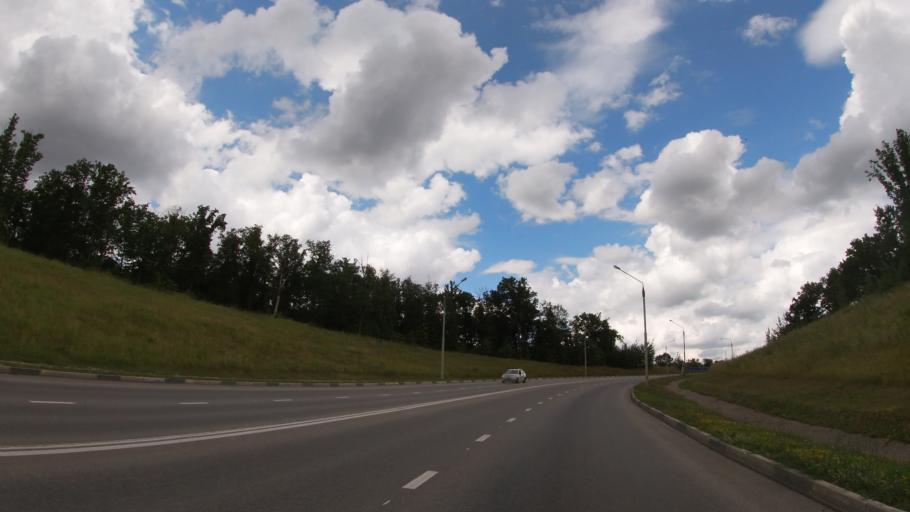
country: RU
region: Belgorod
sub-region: Belgorodskiy Rayon
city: Belgorod
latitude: 50.6235
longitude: 36.6118
